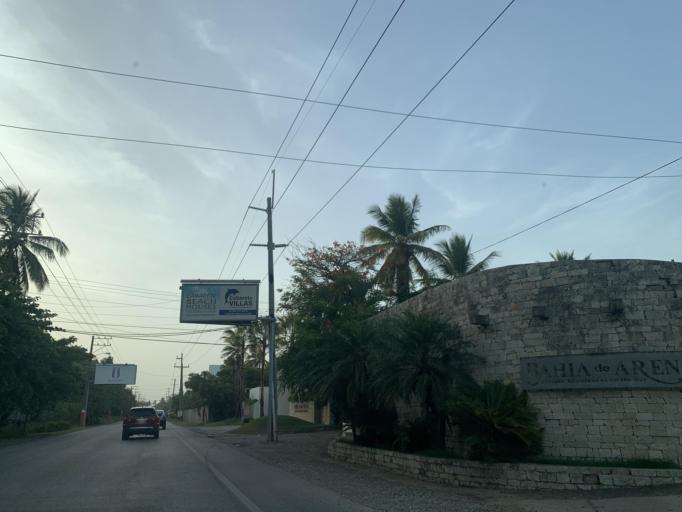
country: DO
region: Puerto Plata
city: Cabarete
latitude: 19.7560
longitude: -70.4182
